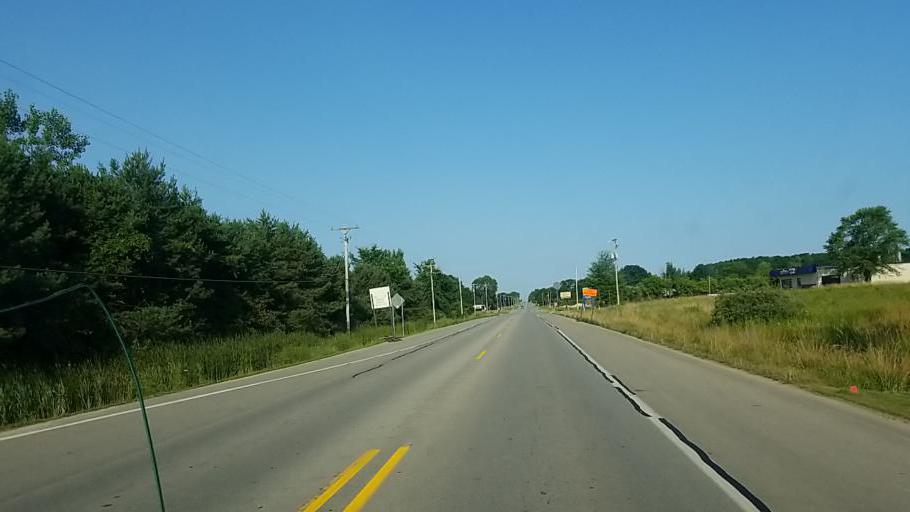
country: US
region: Michigan
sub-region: Newaygo County
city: Fremont
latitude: 43.4672
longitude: -85.9832
